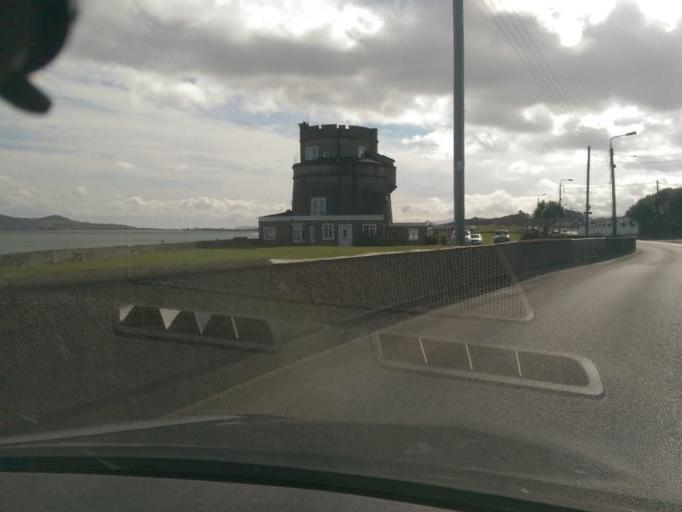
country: IE
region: Leinster
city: Portmarnock
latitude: 53.4366
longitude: -6.1223
